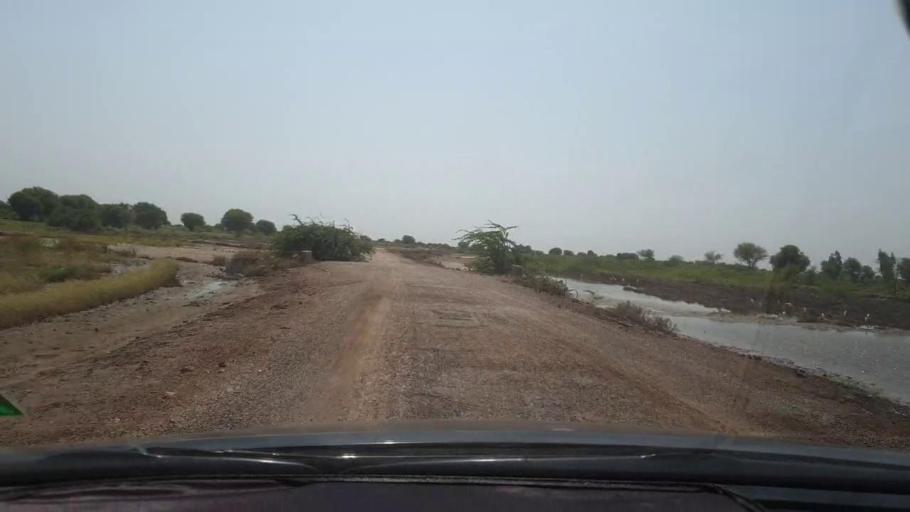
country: PK
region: Sindh
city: Tando Bago
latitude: 24.8078
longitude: 69.1666
